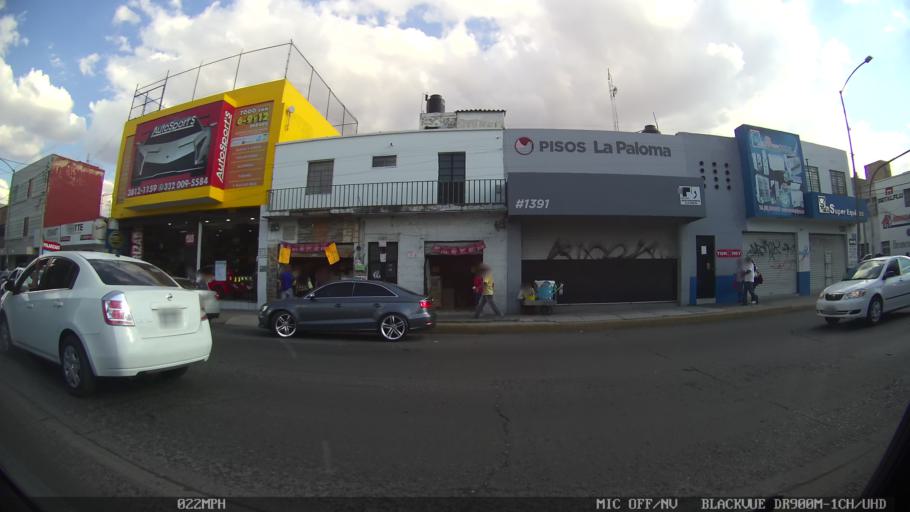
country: MX
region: Jalisco
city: Guadalajara
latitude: 20.6656
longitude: -103.3577
